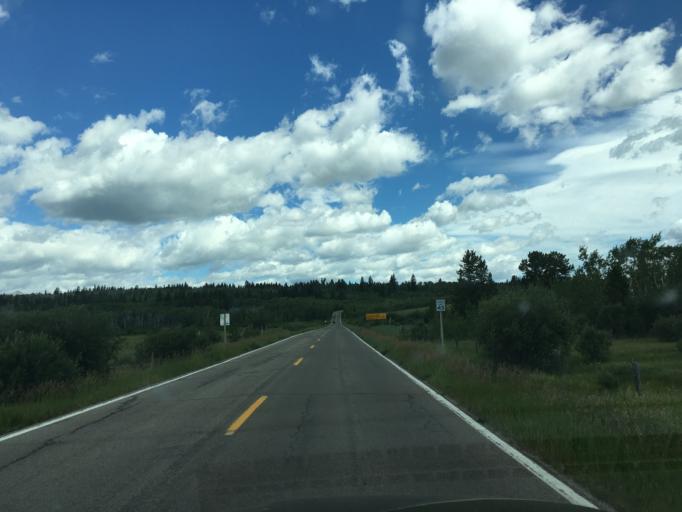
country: US
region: Montana
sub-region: Glacier County
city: South Browning
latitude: 48.4529
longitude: -113.2257
